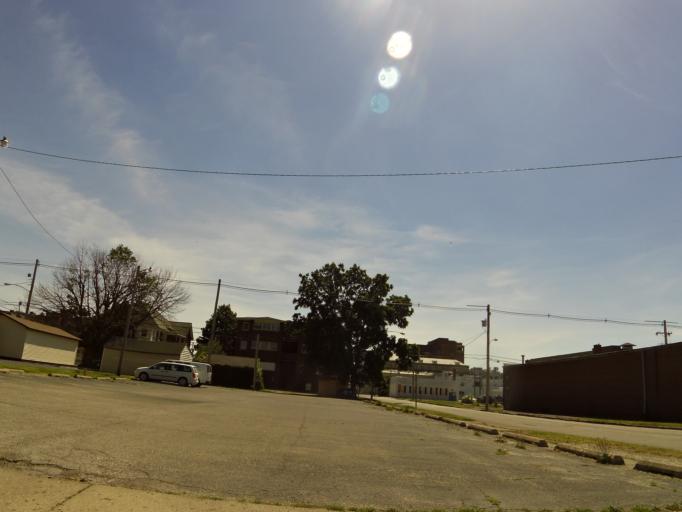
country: US
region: Illinois
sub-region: Vermilion County
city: Danville
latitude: 40.1292
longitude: -87.6327
